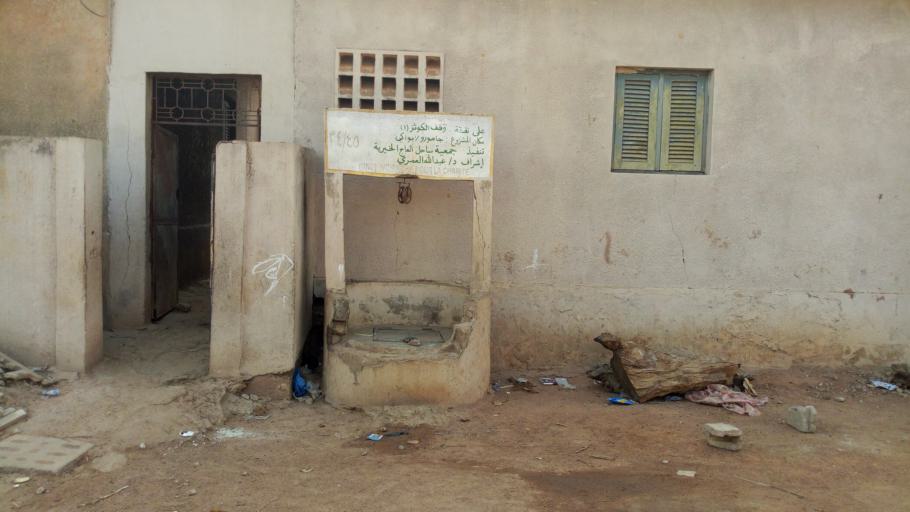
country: CI
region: Vallee du Bandama
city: Bouake
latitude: 7.7023
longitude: -5.0276
